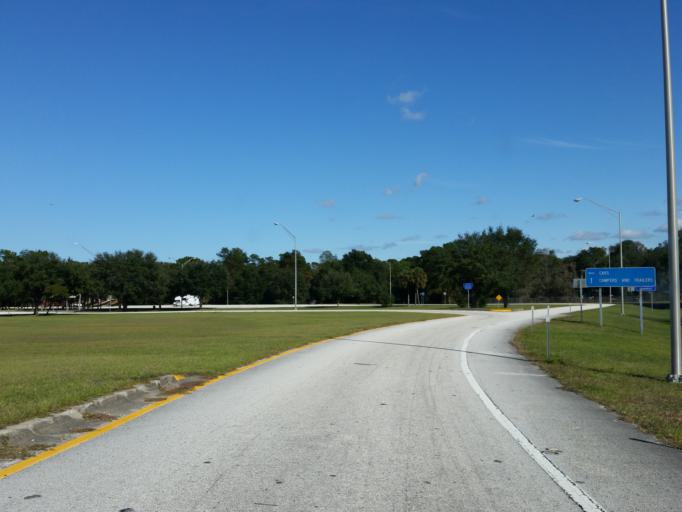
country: US
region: Florida
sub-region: Marion County
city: Ocala
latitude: 29.0912
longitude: -82.1843
